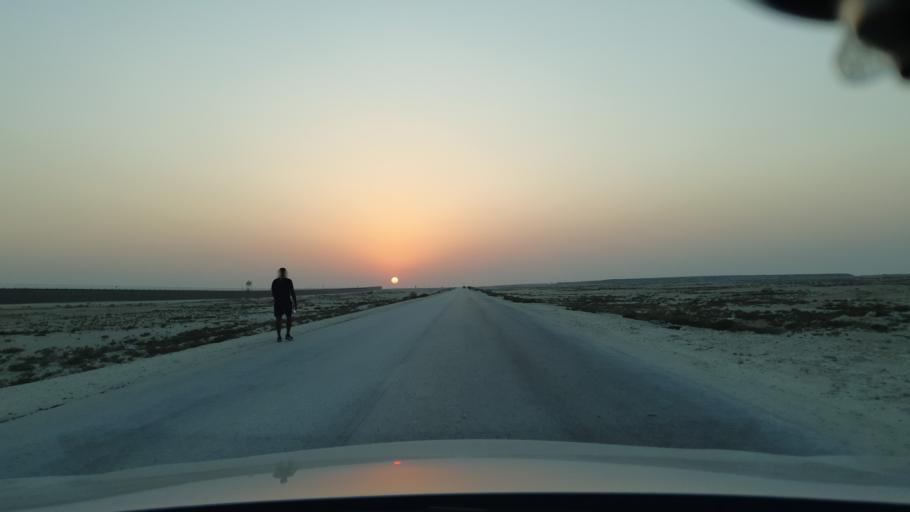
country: BH
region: Central Governorate
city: Dar Kulayb
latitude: 25.9557
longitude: 50.6091
